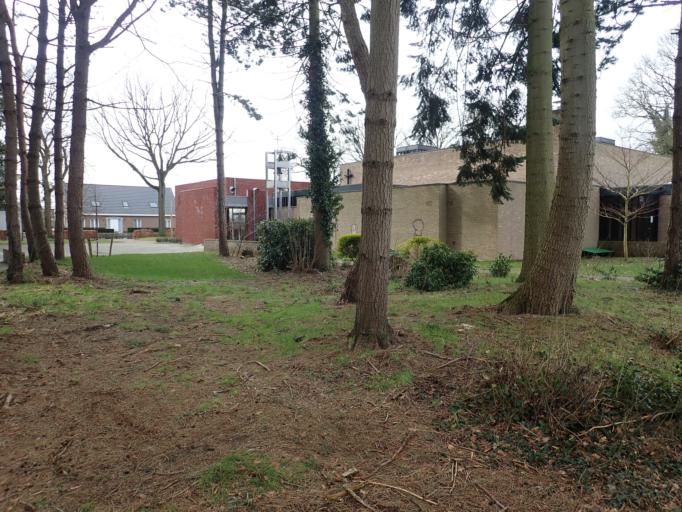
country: BE
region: Flanders
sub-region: Provincie Antwerpen
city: Brecht
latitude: 51.3356
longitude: 4.6653
